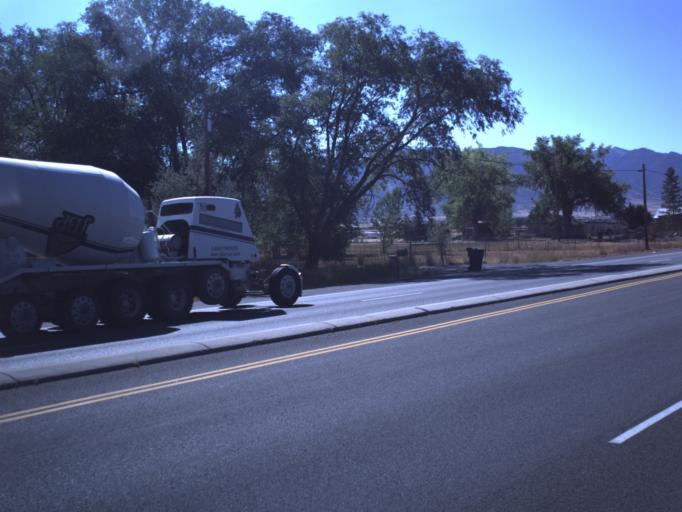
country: US
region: Utah
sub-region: Tooele County
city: Erda
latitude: 40.6103
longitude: -112.2945
